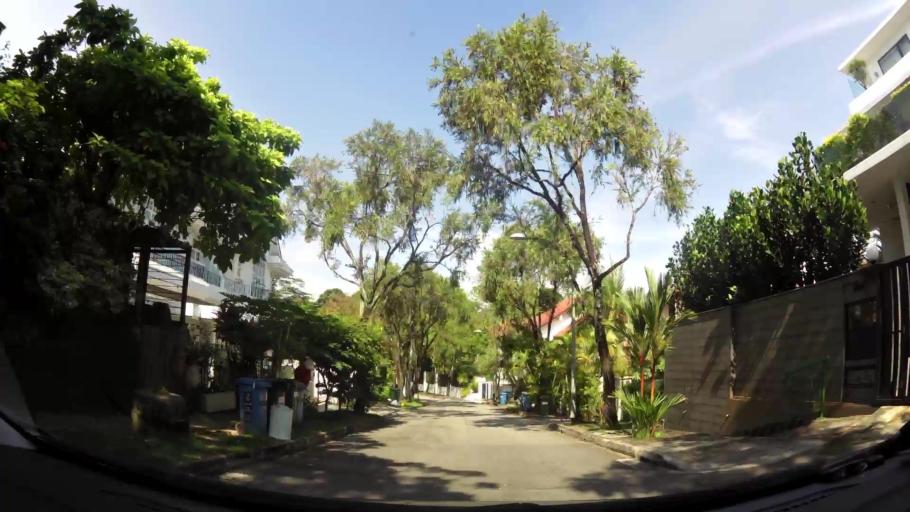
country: SG
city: Singapore
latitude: 1.3641
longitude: 103.8289
